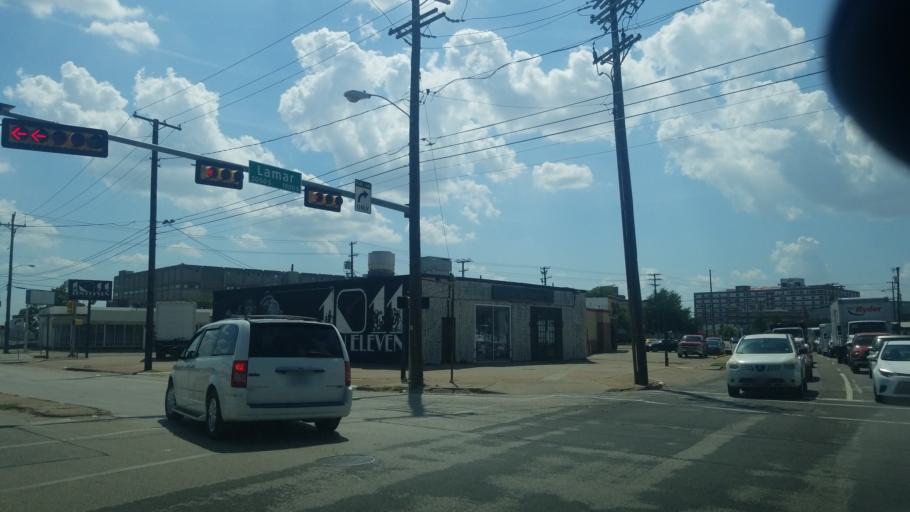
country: US
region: Texas
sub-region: Dallas County
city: Dallas
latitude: 32.7651
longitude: -96.7894
